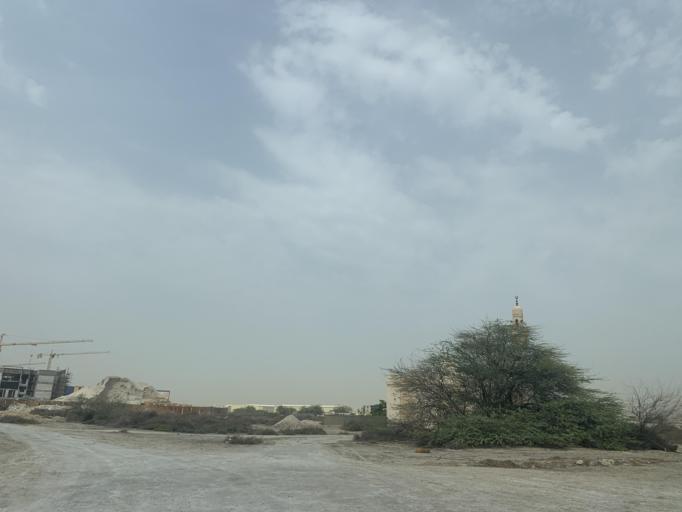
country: BH
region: Northern
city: Madinat `Isa
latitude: 26.1730
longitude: 50.5030
